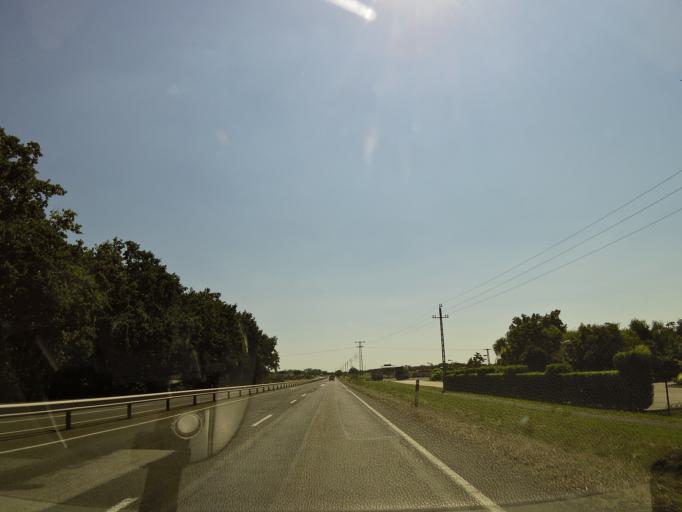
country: HU
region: Jasz-Nagykun-Szolnok
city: Szajol
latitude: 47.1763
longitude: 20.3031
